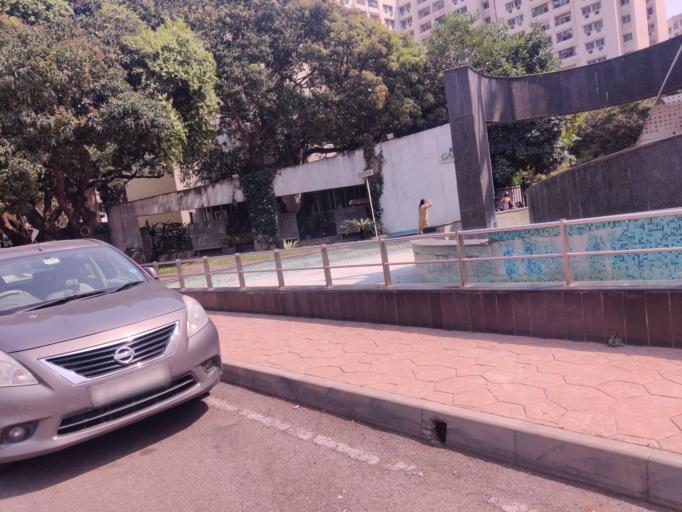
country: IN
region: Karnataka
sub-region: Bangalore Urban
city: Bangalore
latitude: 12.8881
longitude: 77.5781
